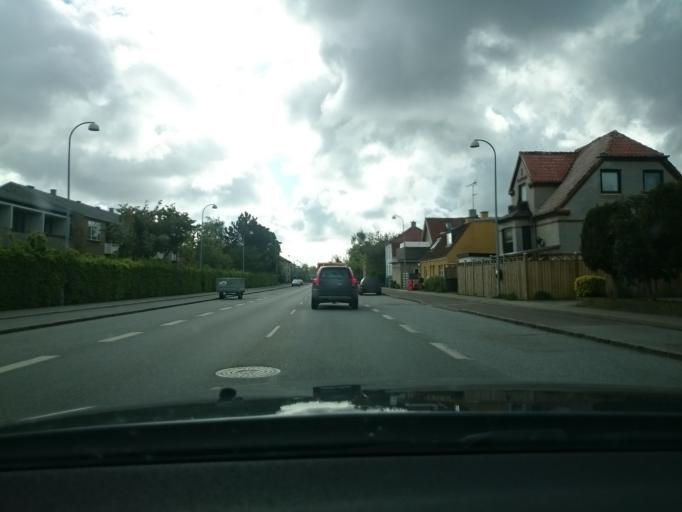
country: DK
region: Capital Region
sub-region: Gladsaxe Municipality
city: Buddinge
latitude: 55.7419
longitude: 12.5086
